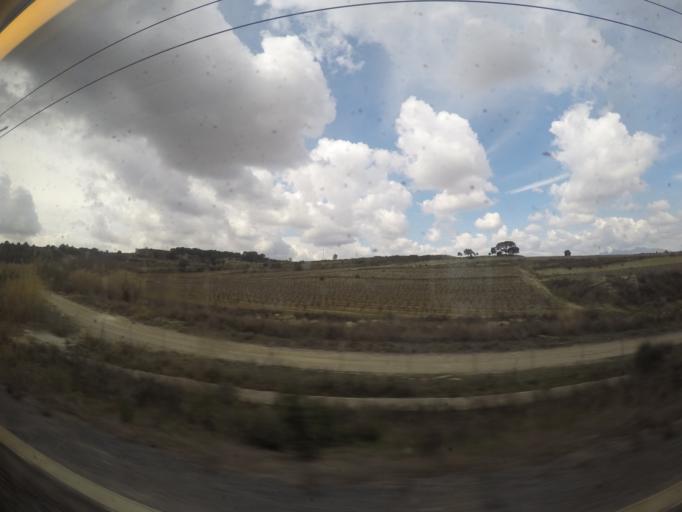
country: ES
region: Catalonia
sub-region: Provincia de Barcelona
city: Sant Llorenc d'Hortons
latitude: 41.4376
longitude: 1.8260
